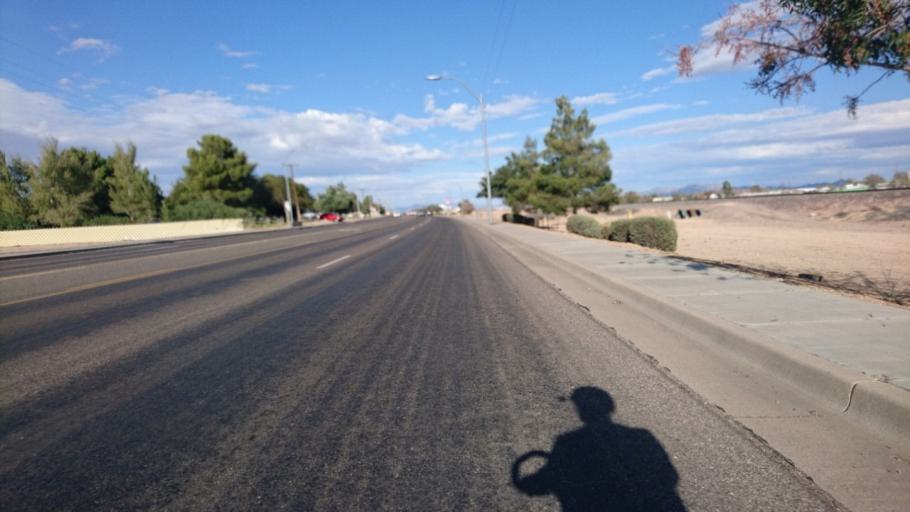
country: US
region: Arizona
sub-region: Mohave County
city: Kingman
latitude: 35.1987
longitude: -114.0270
